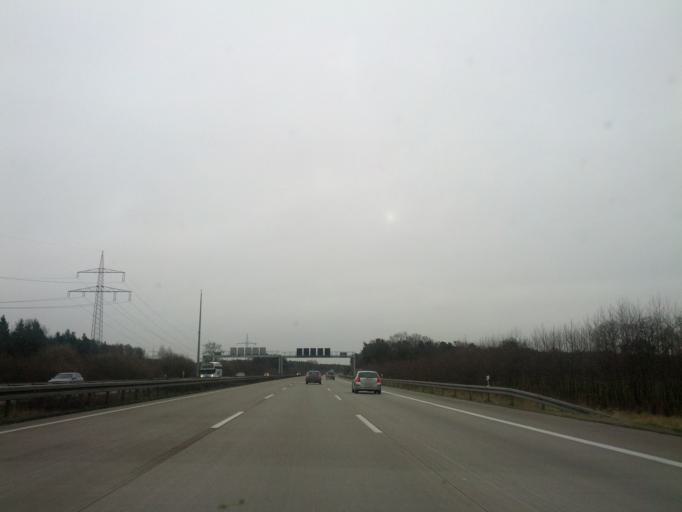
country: DE
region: Lower Saxony
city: Isernhagen Farster Bauerschaft
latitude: 52.5282
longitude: 9.8114
